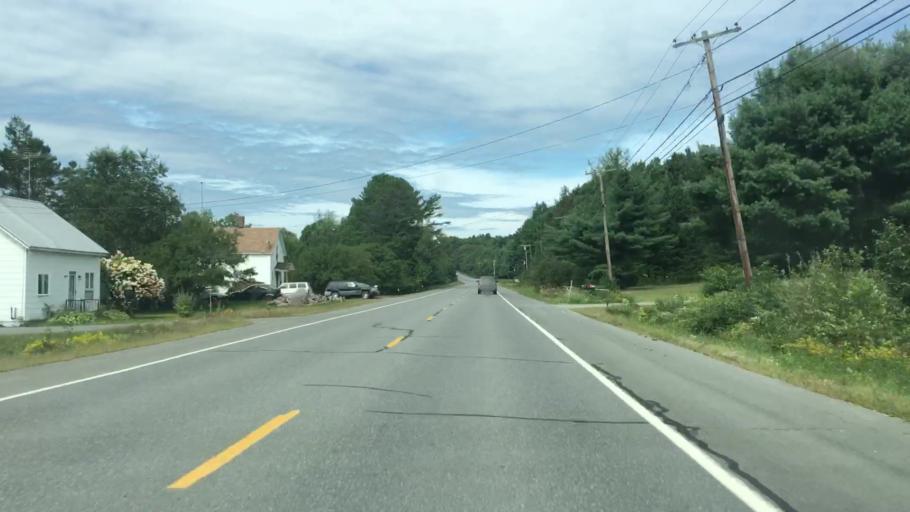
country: US
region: Maine
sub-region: Piscataquis County
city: Milo
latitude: 45.2735
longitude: -69.0012
